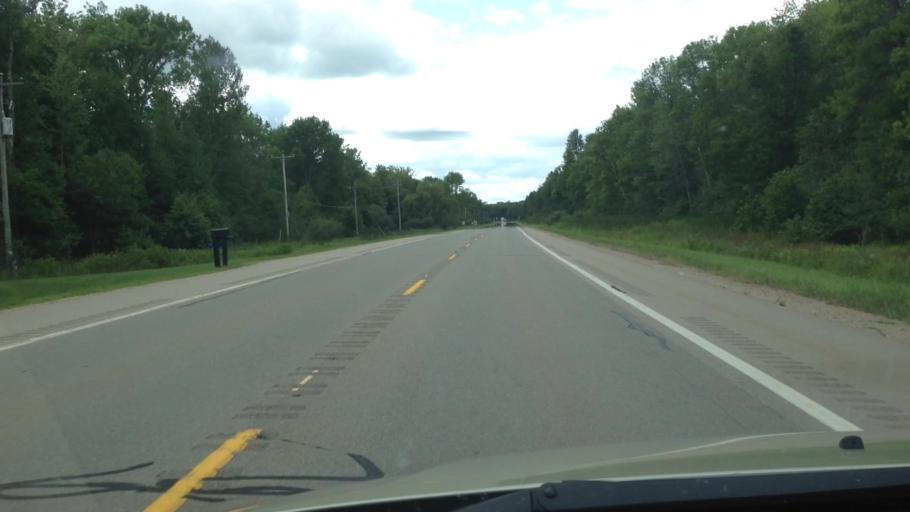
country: US
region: Michigan
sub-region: Menominee County
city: Menominee
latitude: 45.2141
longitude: -87.5237
